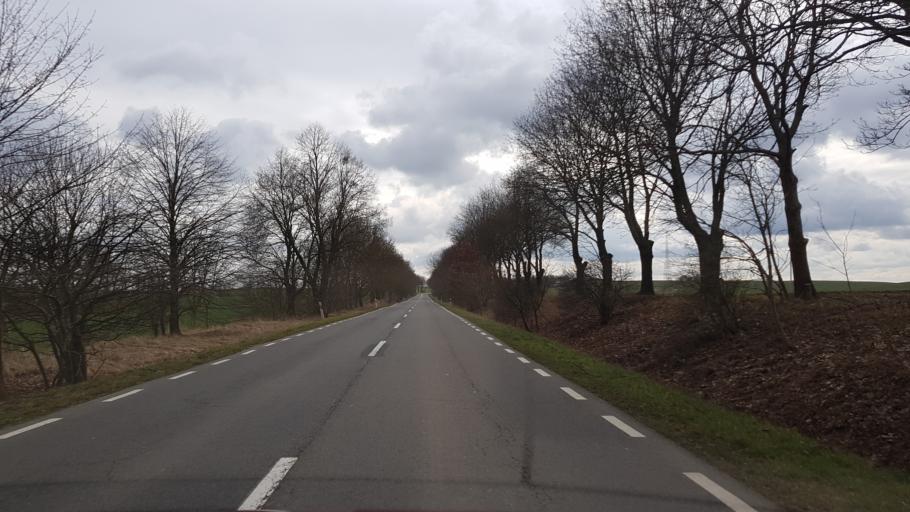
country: PL
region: West Pomeranian Voivodeship
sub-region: Powiat gryfinski
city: Banie
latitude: 53.1585
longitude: 14.6001
